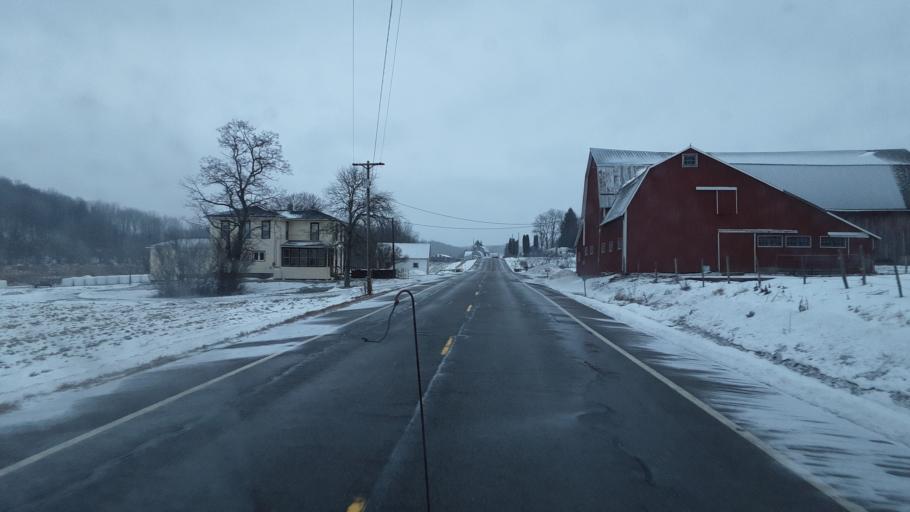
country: US
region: Pennsylvania
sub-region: Tioga County
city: Westfield
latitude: 42.0816
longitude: -77.5417
